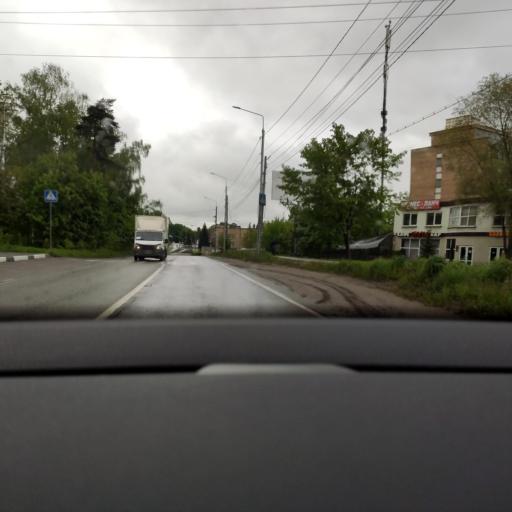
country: RU
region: Moskovskaya
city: Saltykovka
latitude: 55.7344
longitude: 37.9681
